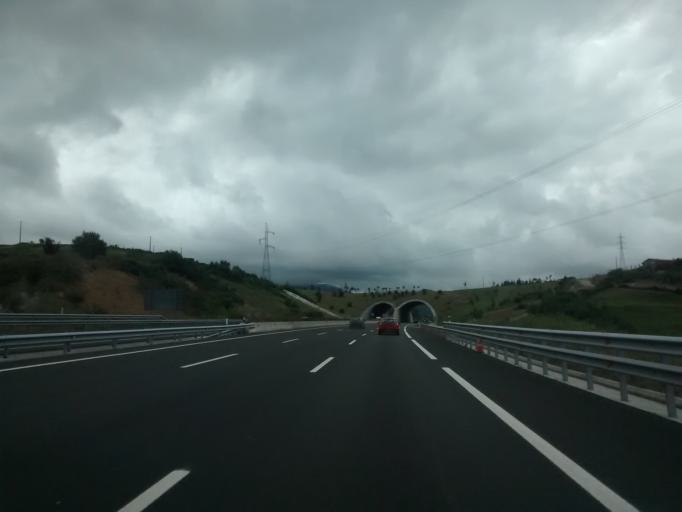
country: ES
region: Cantabria
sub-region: Provincia de Cantabria
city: Molledo
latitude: 43.1549
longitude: -4.0532
